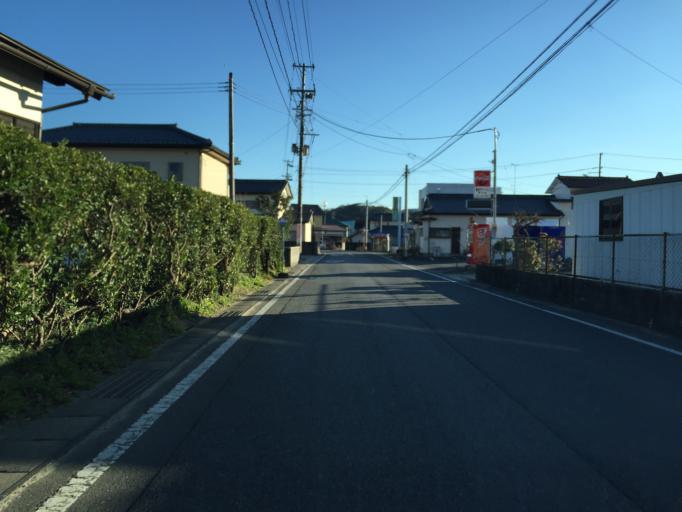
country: JP
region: Fukushima
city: Iwaki
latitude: 37.0837
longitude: 140.8657
